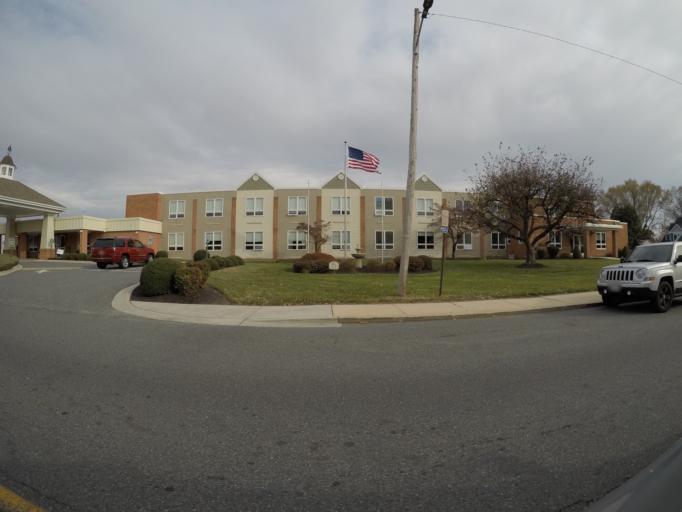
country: US
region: Maryland
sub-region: Harford County
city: Havre de Grace
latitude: 39.5440
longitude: -76.0879
